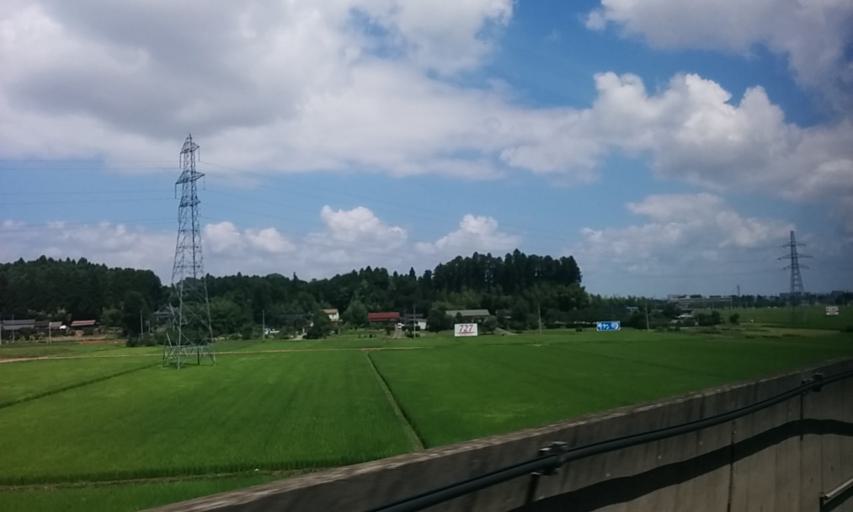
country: JP
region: Miyagi
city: Iwanuma
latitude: 38.1698
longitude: 140.8600
